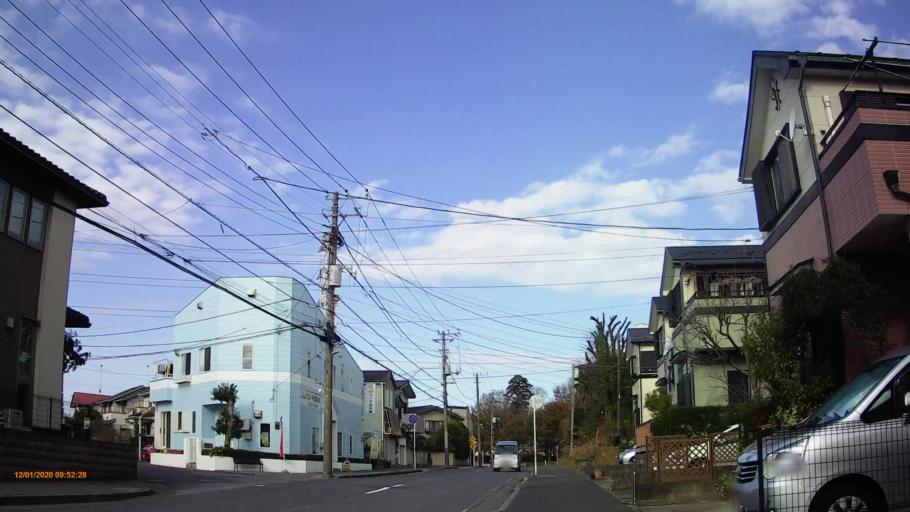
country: JP
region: Chiba
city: Yotsukaido
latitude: 35.6262
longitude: 140.1886
